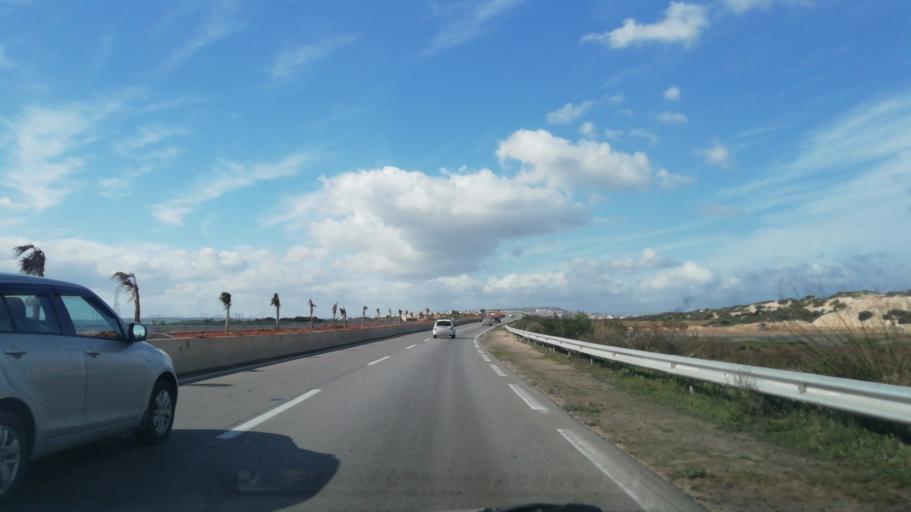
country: DZ
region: Oran
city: Ain el Bya
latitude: 35.7860
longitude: -0.1217
